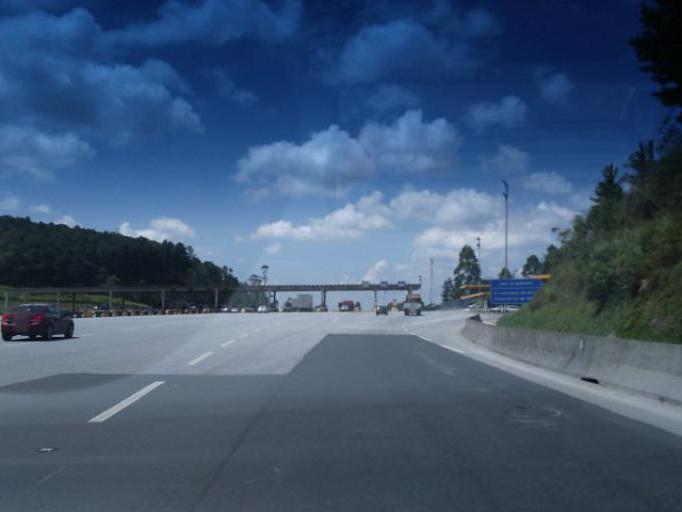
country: BR
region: Sao Paulo
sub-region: Sao Lourenco Da Serra
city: Sao Lourenco da Serra
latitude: -23.7860
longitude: -46.9140
